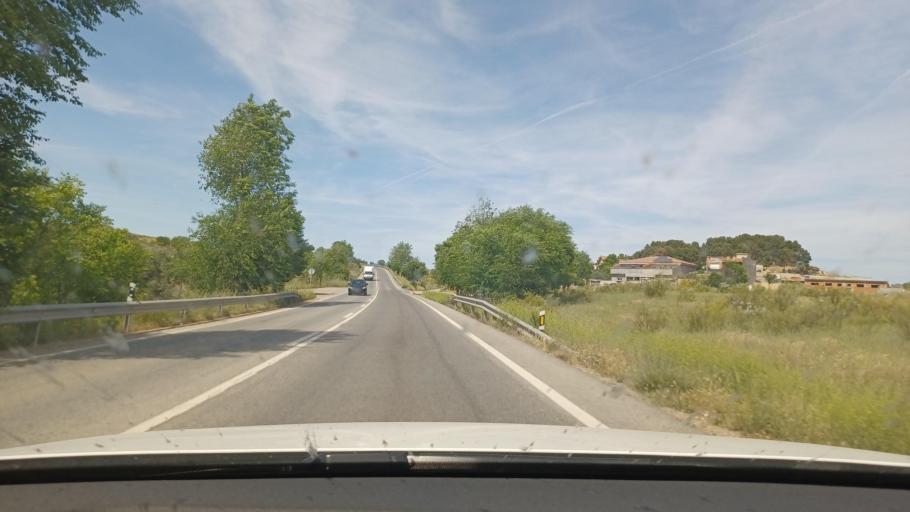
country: ES
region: Madrid
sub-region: Provincia de Madrid
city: Mejorada del Campo
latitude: 40.4064
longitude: -3.4797
